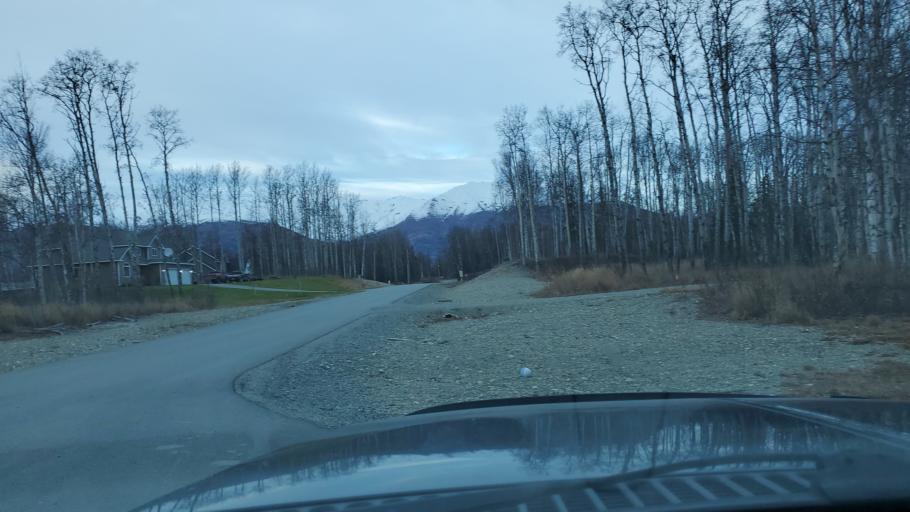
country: US
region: Alaska
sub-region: Matanuska-Susitna Borough
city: Lakes
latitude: 61.6554
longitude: -149.3034
